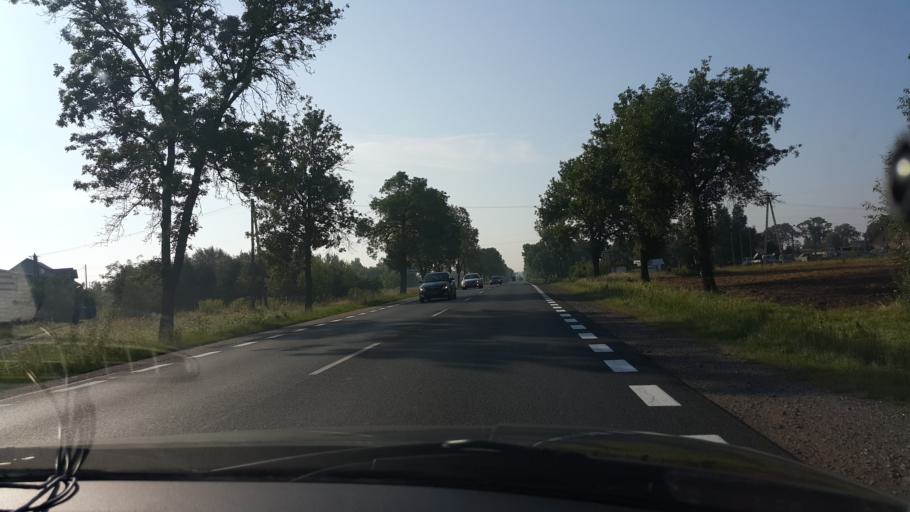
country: PL
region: Masovian Voivodeship
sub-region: Powiat radomski
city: Jedlnia-Letnisko
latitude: 51.3967
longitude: 21.2629
